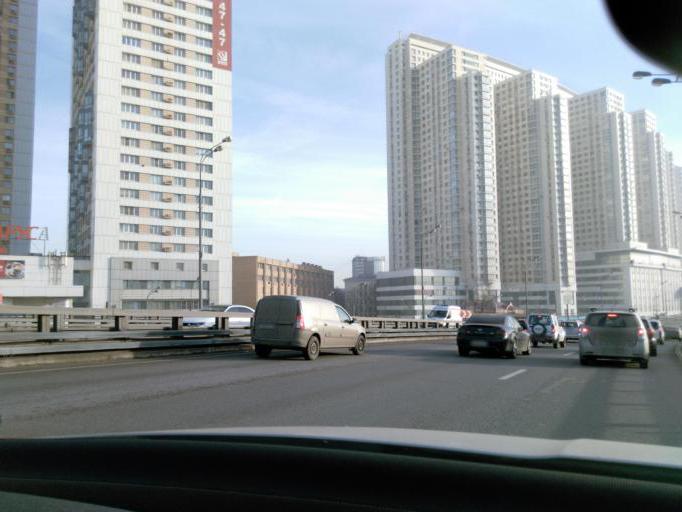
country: RU
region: Moskovskaya
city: Presnenskiy
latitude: 55.7731
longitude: 37.5460
